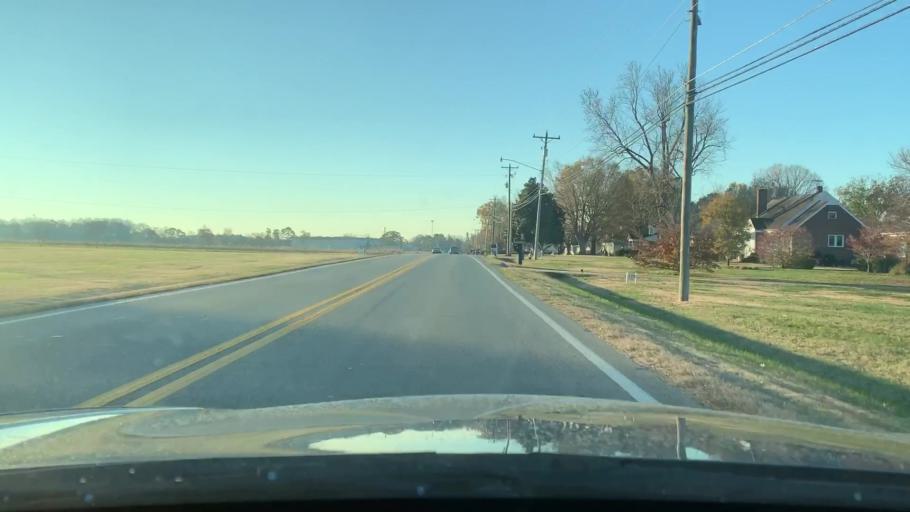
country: US
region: North Carolina
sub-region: Alamance County
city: Green Level
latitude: 36.1075
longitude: -79.3531
